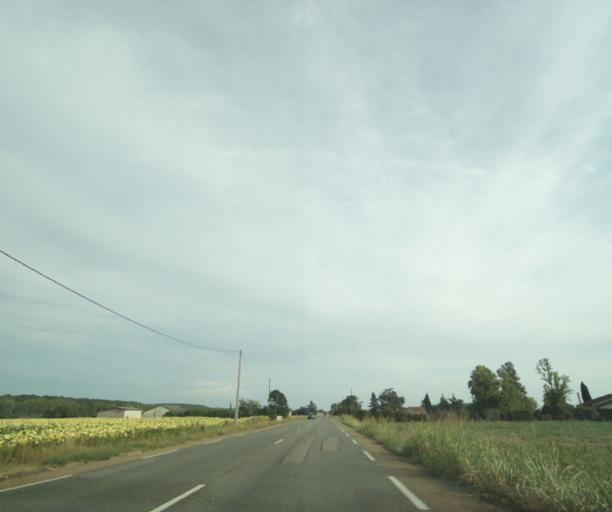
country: FR
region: Midi-Pyrenees
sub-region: Departement du Tarn-et-Garonne
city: Verdun-sur-Garonne
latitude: 43.8750
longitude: 1.2605
